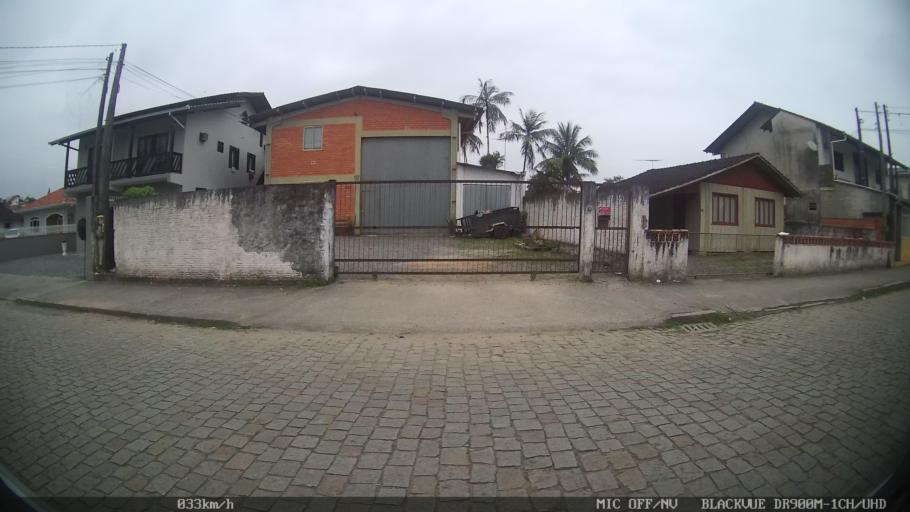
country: BR
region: Santa Catarina
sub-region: Joinville
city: Joinville
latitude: -26.3438
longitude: -48.8546
